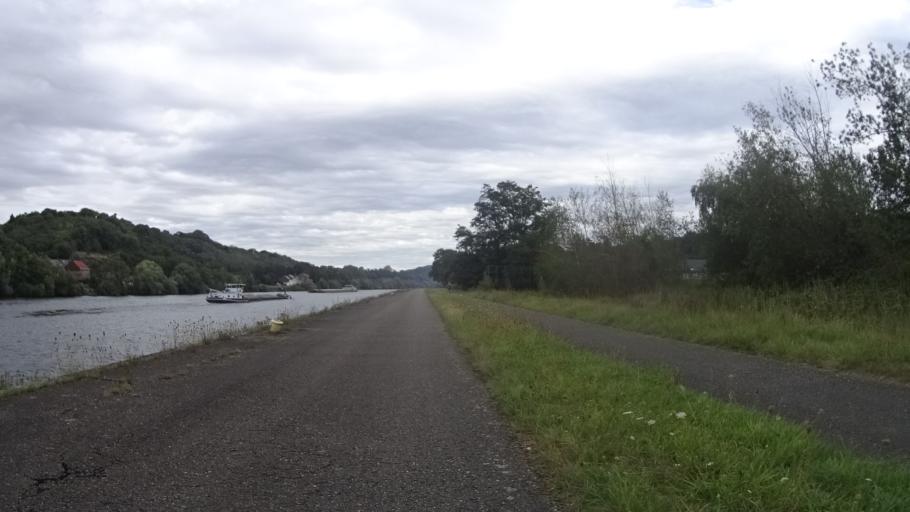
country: BE
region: Wallonia
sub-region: Province de Liege
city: Wanze
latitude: 50.5145
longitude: 5.1739
